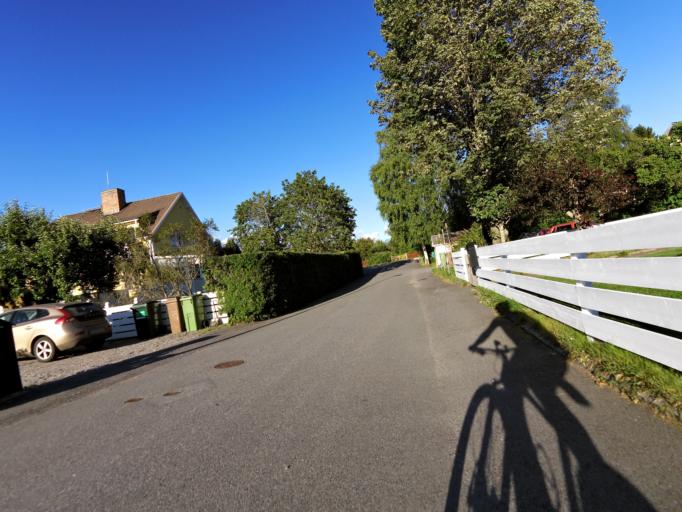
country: SE
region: Gaevleborg
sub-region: Gavle Kommun
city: Gavle
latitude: 60.7109
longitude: 17.1453
